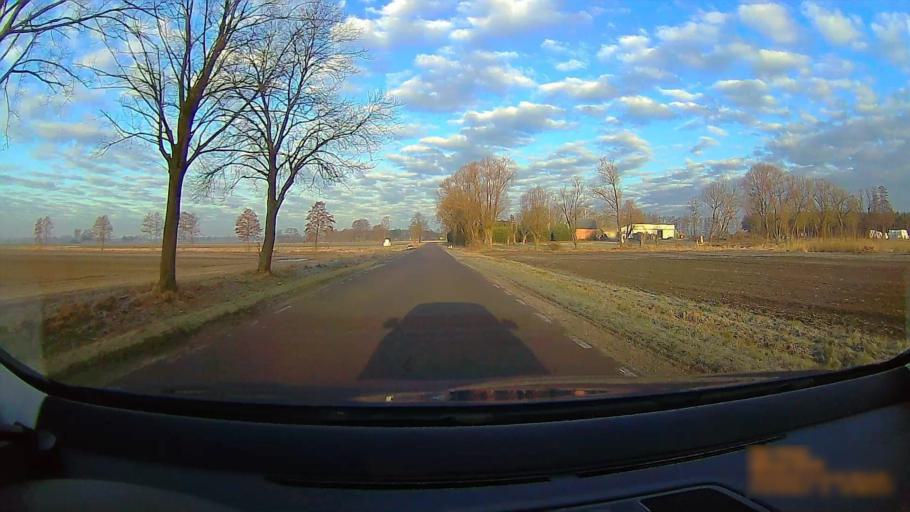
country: PL
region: Greater Poland Voivodeship
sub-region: Powiat koninski
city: Rychwal
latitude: 52.0996
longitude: 18.1033
